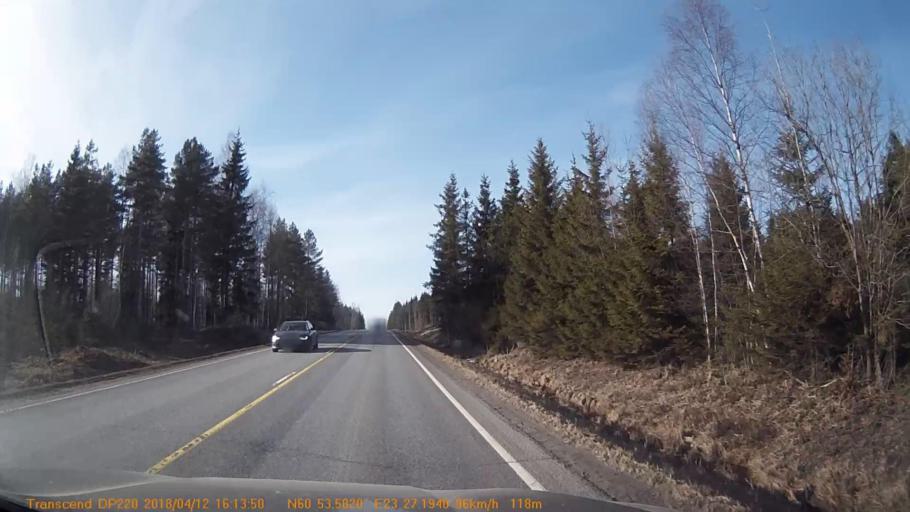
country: FI
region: Haeme
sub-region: Forssa
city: Humppila
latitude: 60.8931
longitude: 23.4530
